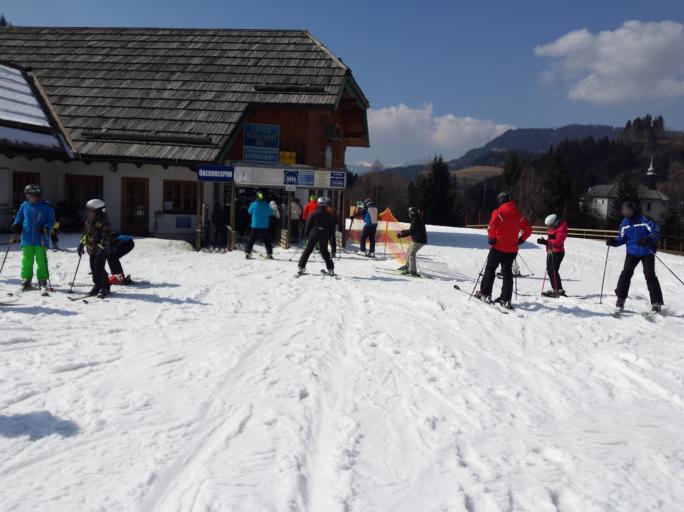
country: AT
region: Carinthia
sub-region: Politischer Bezirk Villach Land
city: Arriach
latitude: 46.7298
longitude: 13.9144
